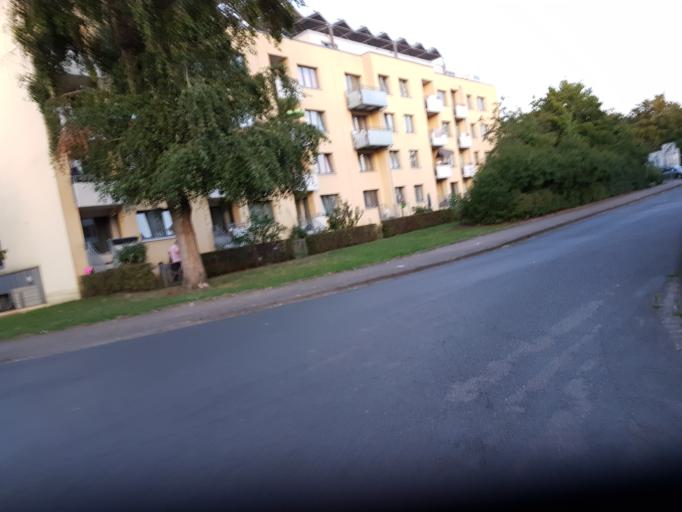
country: DE
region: Lower Saxony
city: Langenhagen
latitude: 52.4108
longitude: 9.7565
